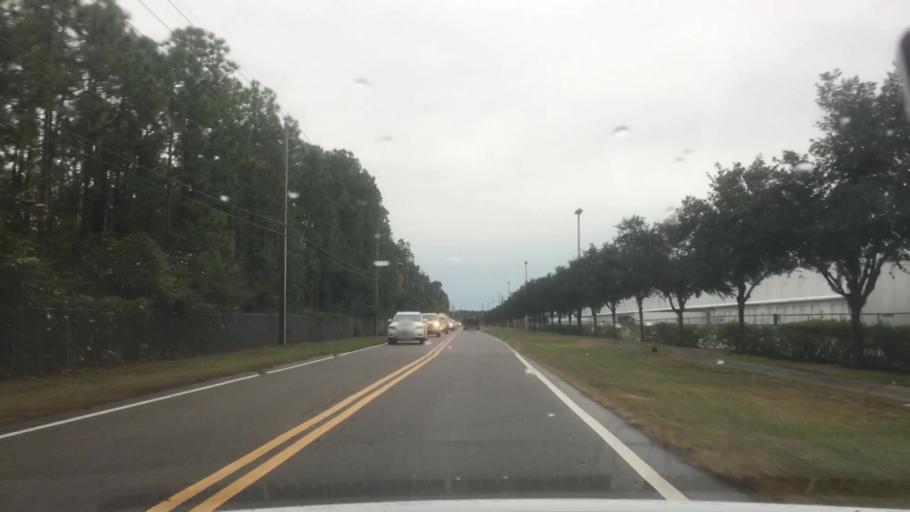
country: US
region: Florida
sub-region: Duval County
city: Jacksonville
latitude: 30.4468
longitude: -81.5582
